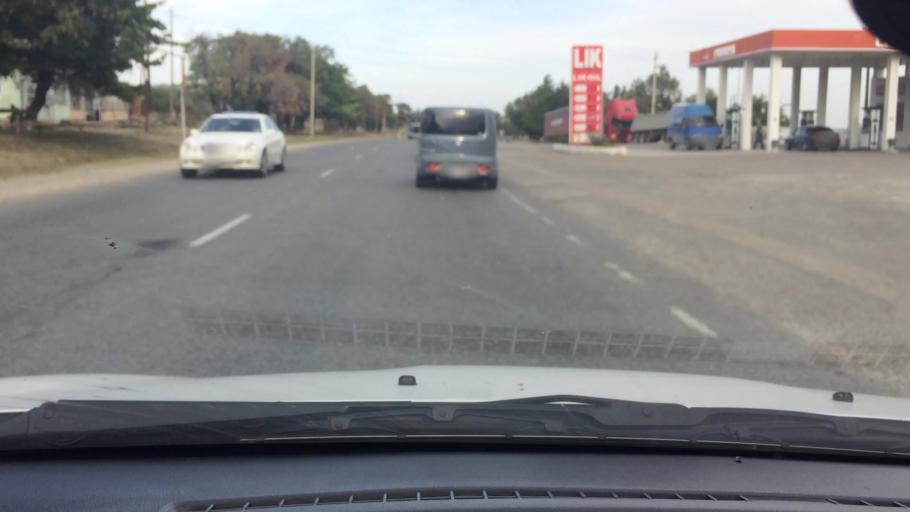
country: GE
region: T'bilisi
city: Tbilisi
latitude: 41.6422
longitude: 44.8371
